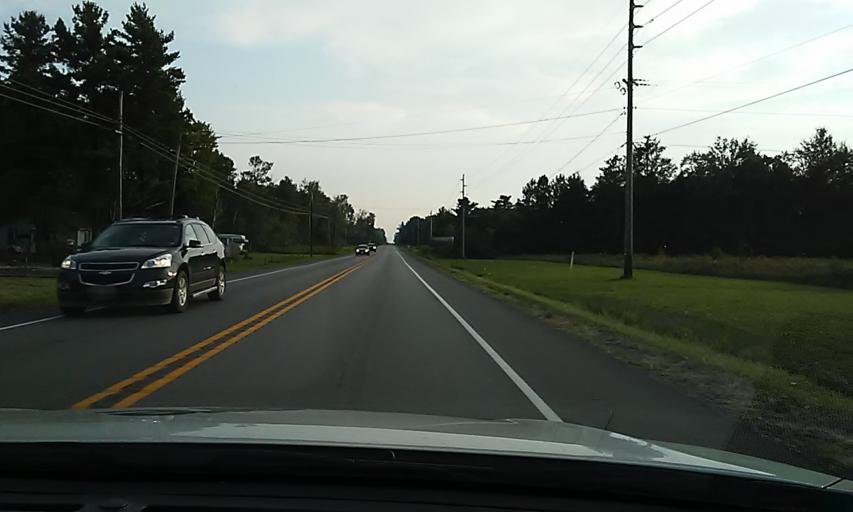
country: US
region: Pennsylvania
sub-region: Forest County
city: Marienville
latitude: 41.4815
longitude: -79.1071
